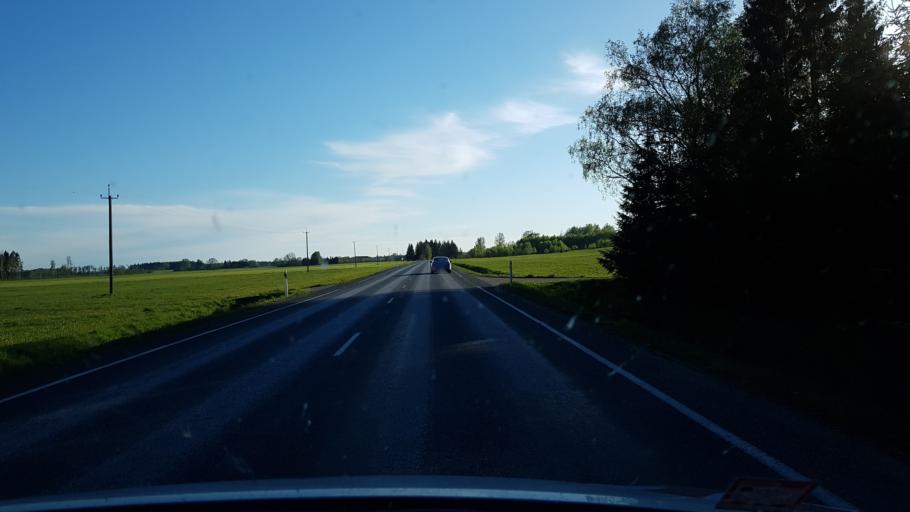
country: EE
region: Jaervamaa
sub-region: Tueri vald
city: Sarevere
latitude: 58.7619
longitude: 25.4015
